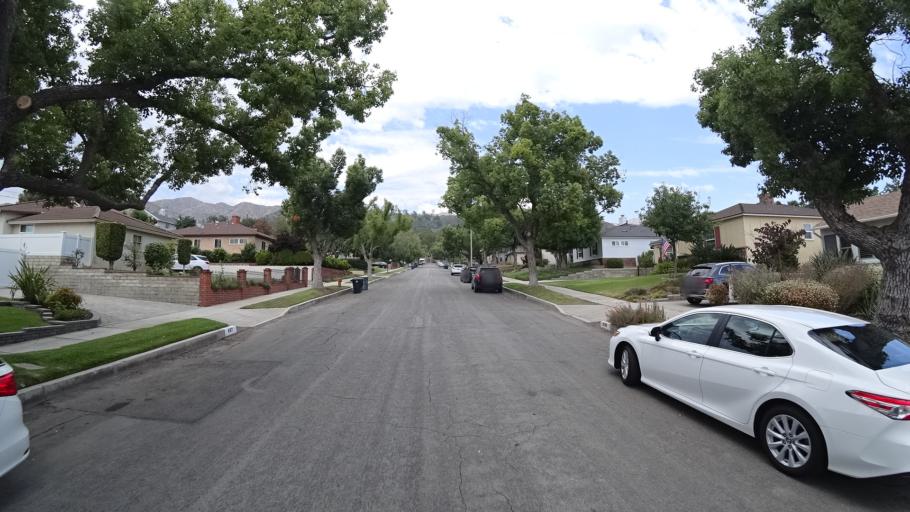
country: US
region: California
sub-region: Los Angeles County
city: Burbank
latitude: 34.1991
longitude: -118.3148
